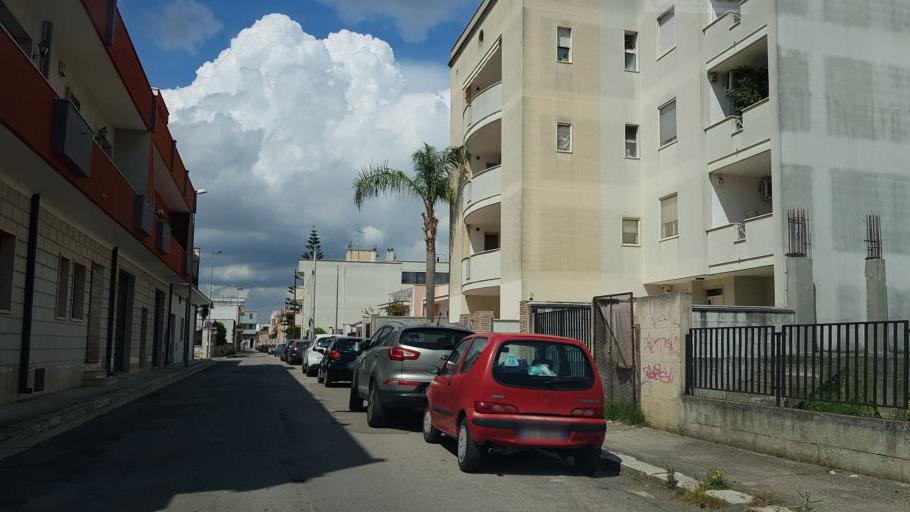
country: IT
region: Apulia
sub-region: Provincia di Brindisi
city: Mesagne
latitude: 40.5553
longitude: 17.8160
